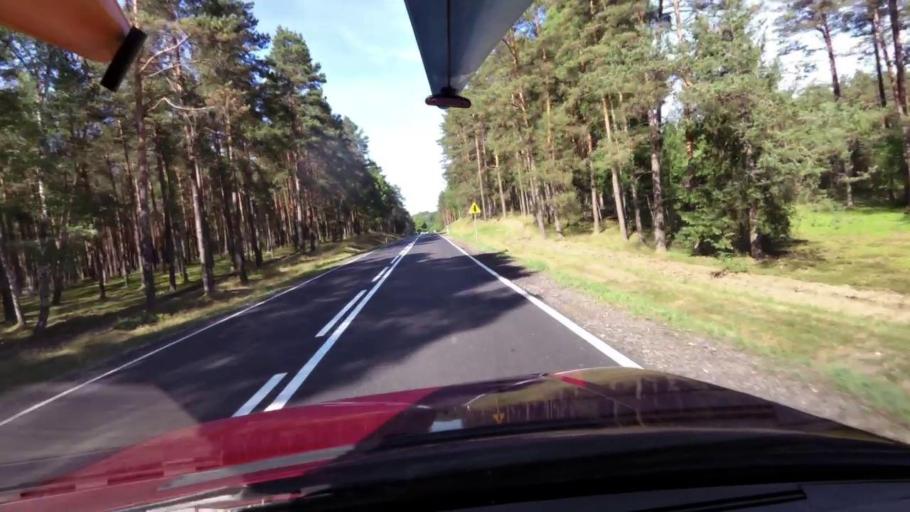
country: PL
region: Pomeranian Voivodeship
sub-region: Powiat bytowski
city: Trzebielino
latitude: 54.1405
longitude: 17.0263
